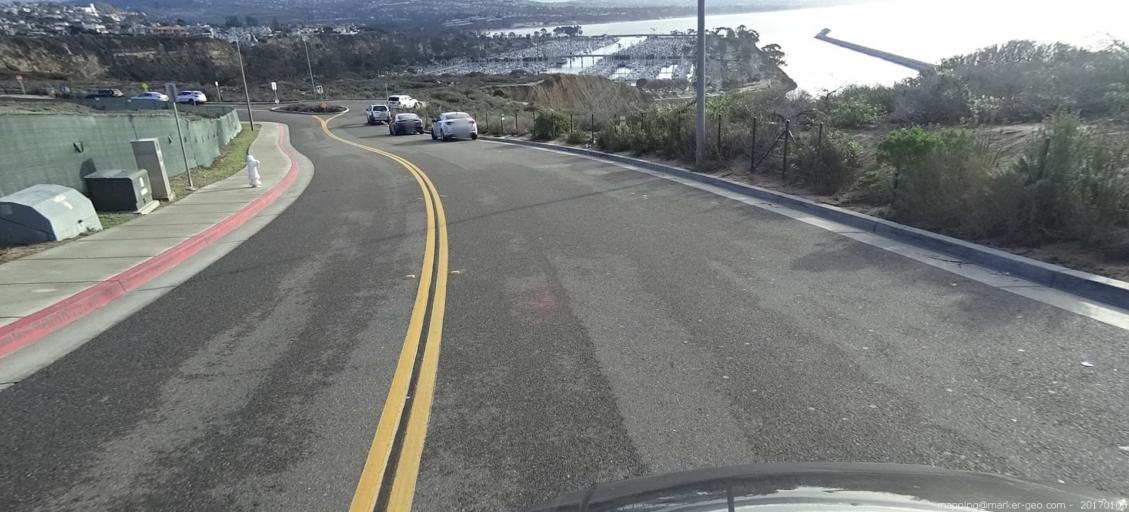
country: US
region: California
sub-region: Orange County
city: Dana Point
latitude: 33.4611
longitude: -117.7105
